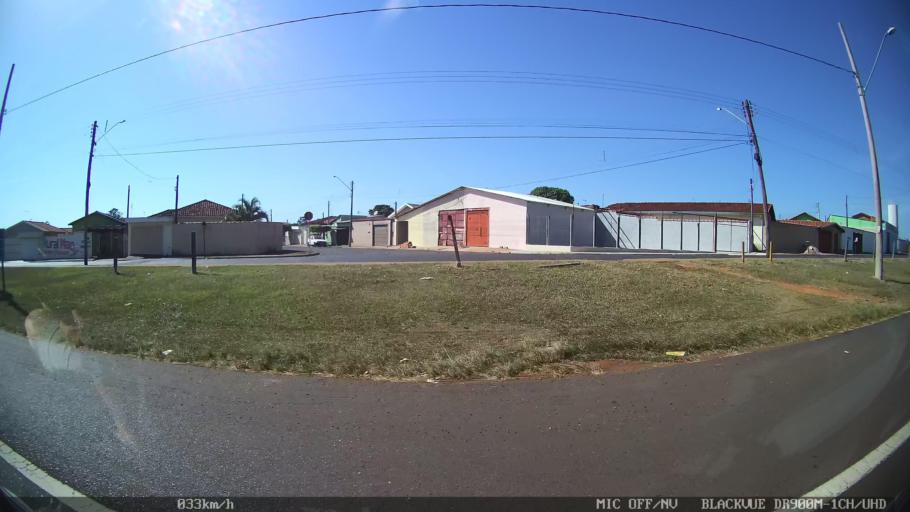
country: BR
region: Sao Paulo
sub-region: Batatais
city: Batatais
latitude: -20.9148
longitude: -47.5834
